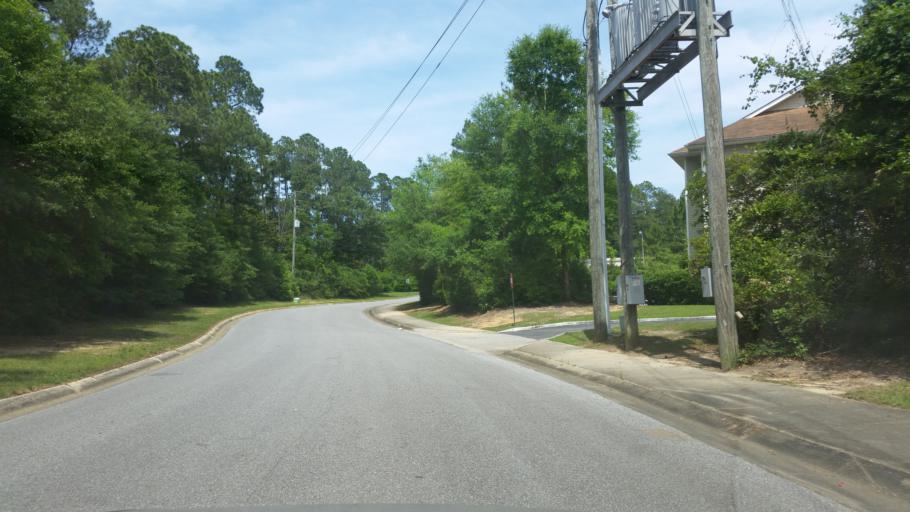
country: US
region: Florida
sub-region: Escambia County
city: Ferry Pass
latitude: 30.5401
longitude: -87.2213
